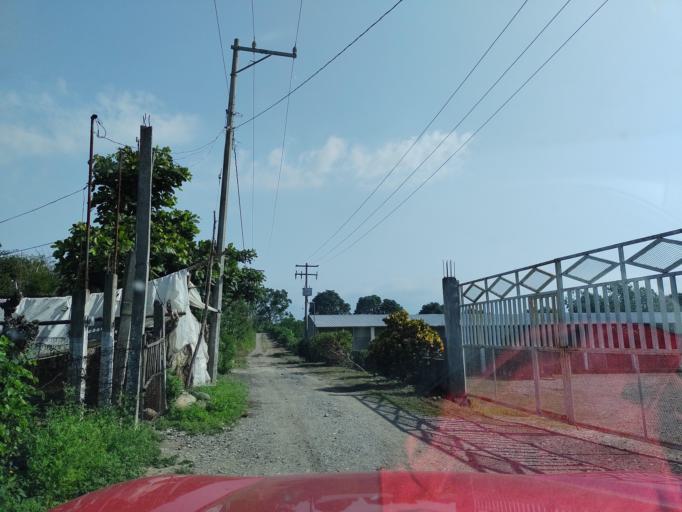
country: MX
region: Puebla
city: Espinal
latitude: 20.2728
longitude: -97.3302
